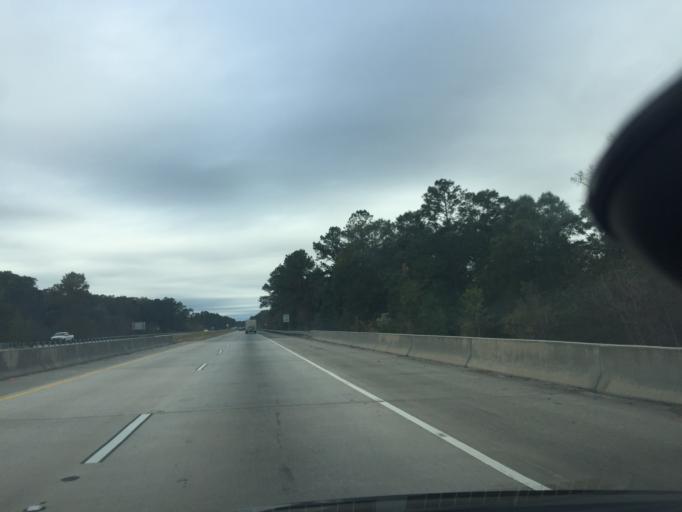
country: US
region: Georgia
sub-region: Chatham County
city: Bloomingdale
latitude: 32.1346
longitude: -81.4018
